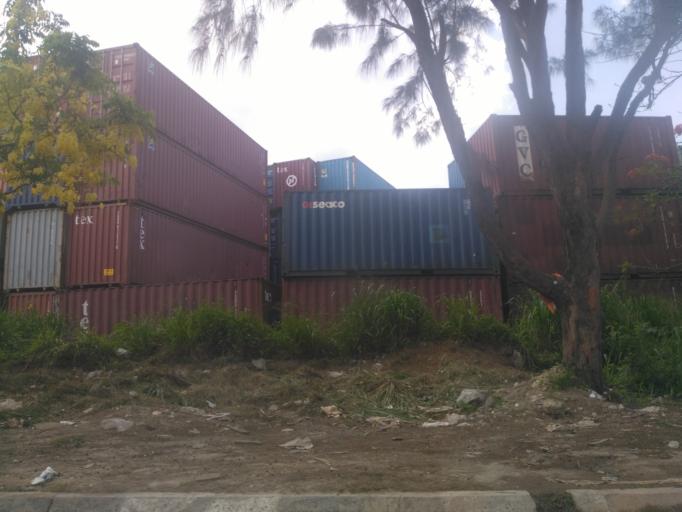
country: TZ
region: Zanzibar Urban/West
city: Zanzibar
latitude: -6.1568
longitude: 39.1970
